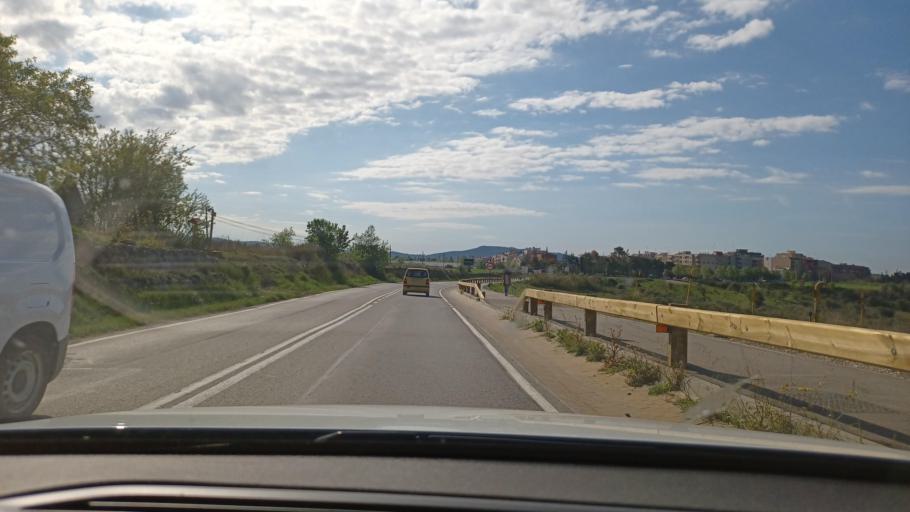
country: ES
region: Catalonia
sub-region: Provincia de Barcelona
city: Vilafranca del Penedes
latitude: 41.3597
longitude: 1.6983
